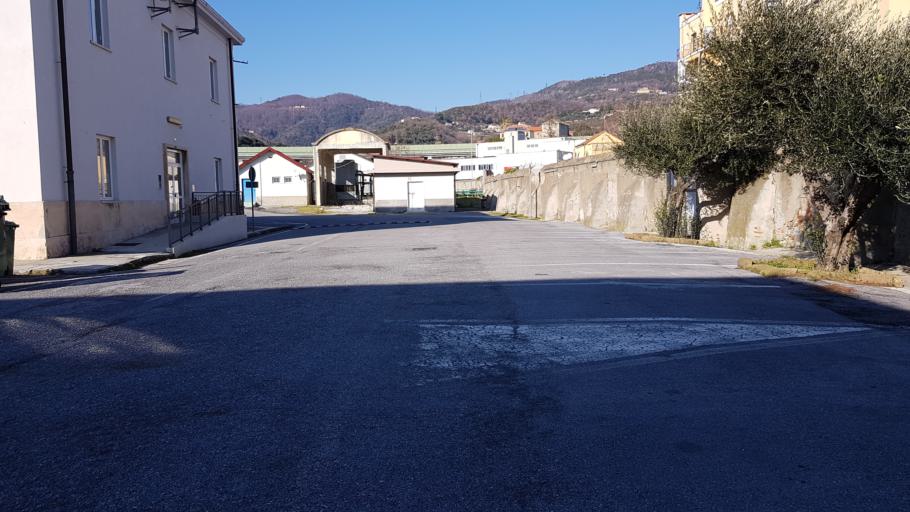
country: IT
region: Liguria
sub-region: Provincia di Savona
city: Savona
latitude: 44.3009
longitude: 8.4518
